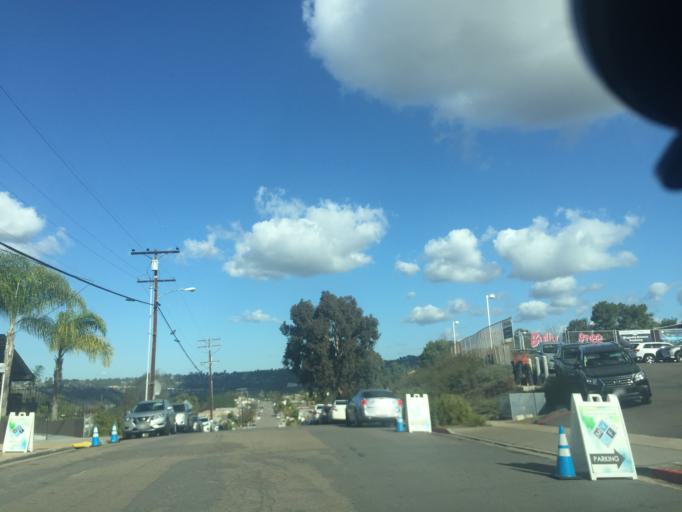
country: US
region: California
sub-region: San Diego County
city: La Mesa
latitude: 32.7917
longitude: -117.0880
